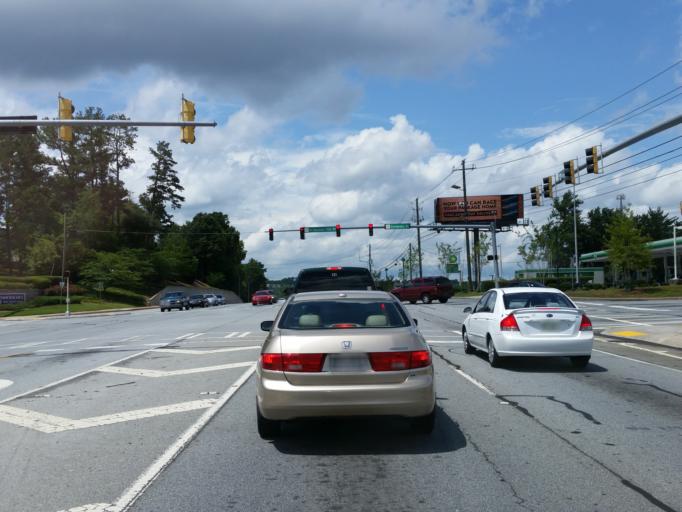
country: US
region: Georgia
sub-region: Fulton County
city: Roswell
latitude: 33.9968
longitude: -84.3508
